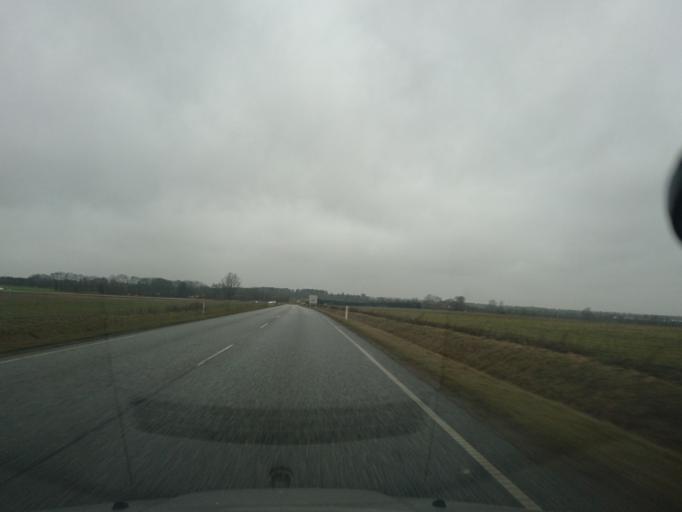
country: DK
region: South Denmark
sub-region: Billund Kommune
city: Billund
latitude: 55.7144
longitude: 9.2082
